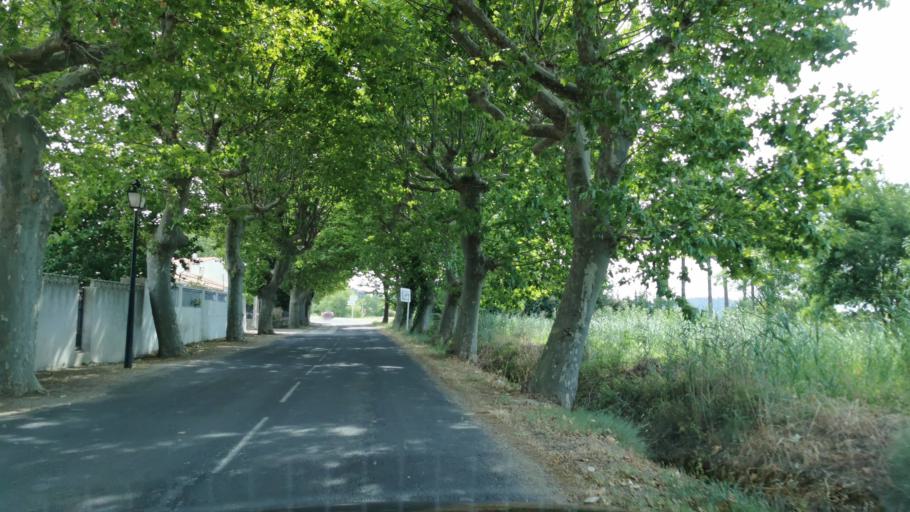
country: FR
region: Languedoc-Roussillon
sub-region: Departement de l'Herault
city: Olonzac
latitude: 43.2663
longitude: 2.7240
